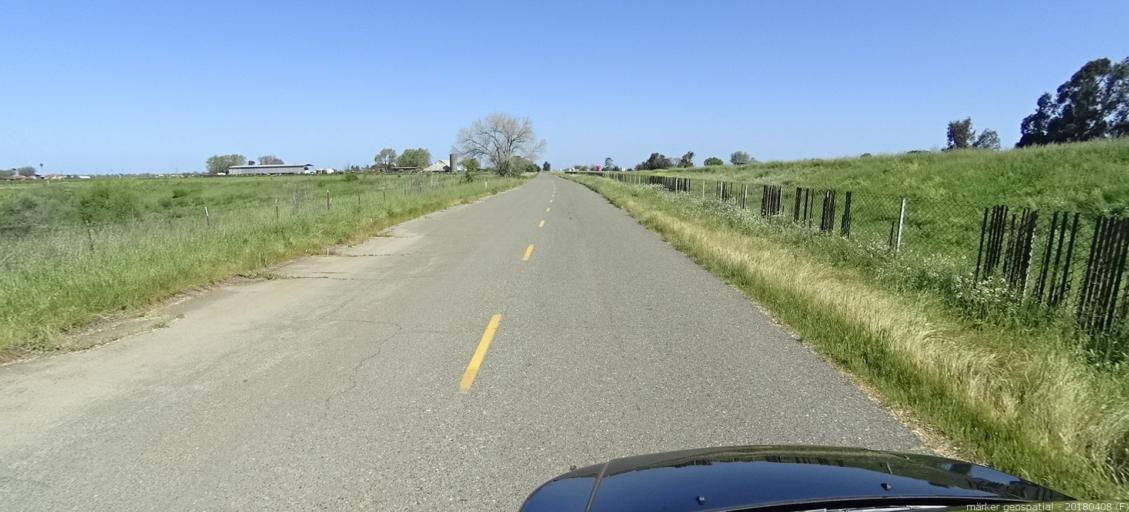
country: US
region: California
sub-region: Sacramento County
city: Walnut Grove
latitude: 38.3234
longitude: -121.4666
